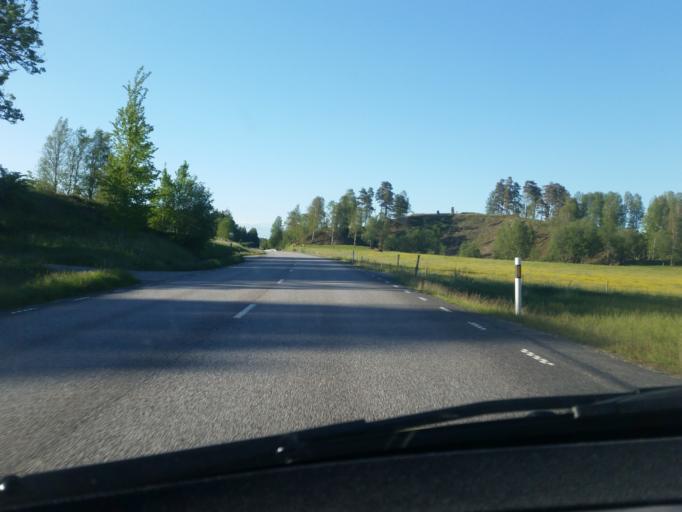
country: SE
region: Vaestra Goetaland
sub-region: Fargelanda Kommun
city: Faergelanda
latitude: 58.5501
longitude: 11.9921
